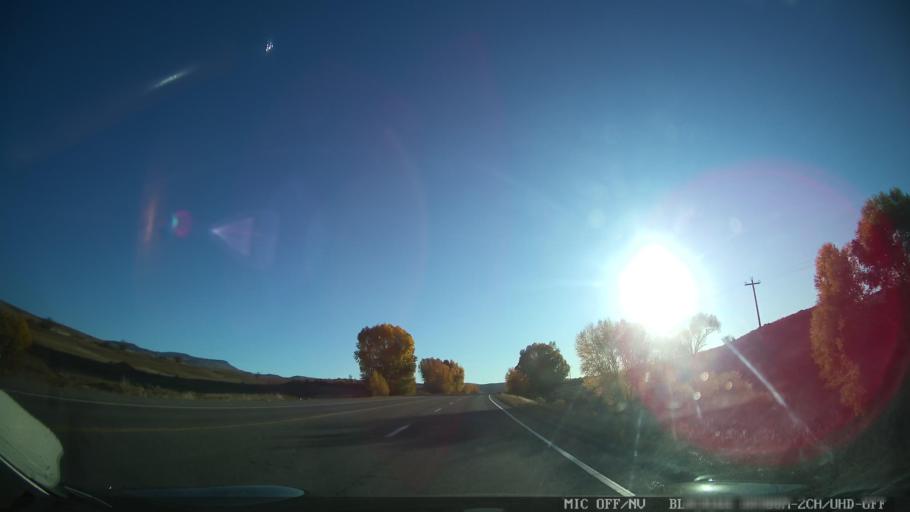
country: US
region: Colorado
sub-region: Grand County
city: Hot Sulphur Springs
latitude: 40.0675
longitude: -106.2275
